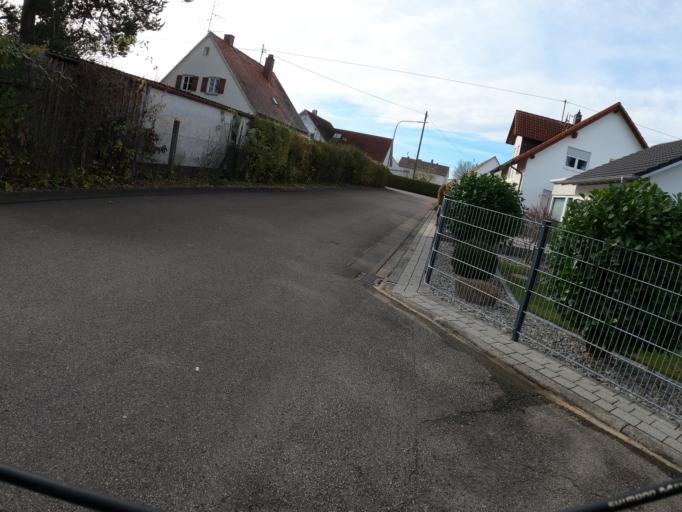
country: DE
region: Bavaria
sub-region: Swabia
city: Nersingen
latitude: 48.4306
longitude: 10.1628
